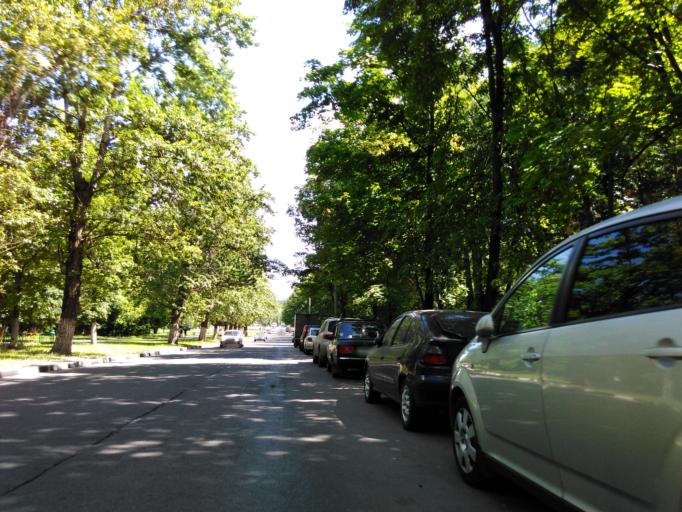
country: RU
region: Moscow
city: Novyye Cheremushki
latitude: 55.6905
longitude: 37.5914
